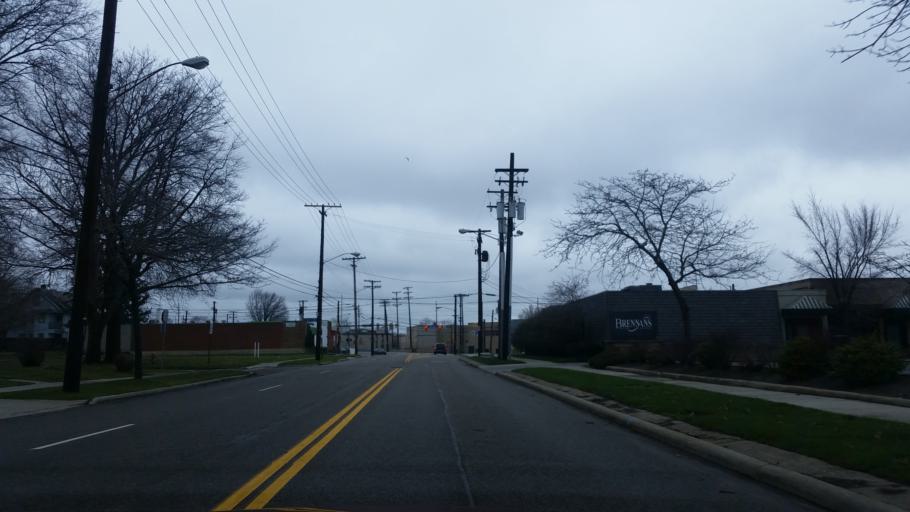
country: US
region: Ohio
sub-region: Cuyahoga County
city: Lakewood
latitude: 41.4651
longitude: -81.7810
